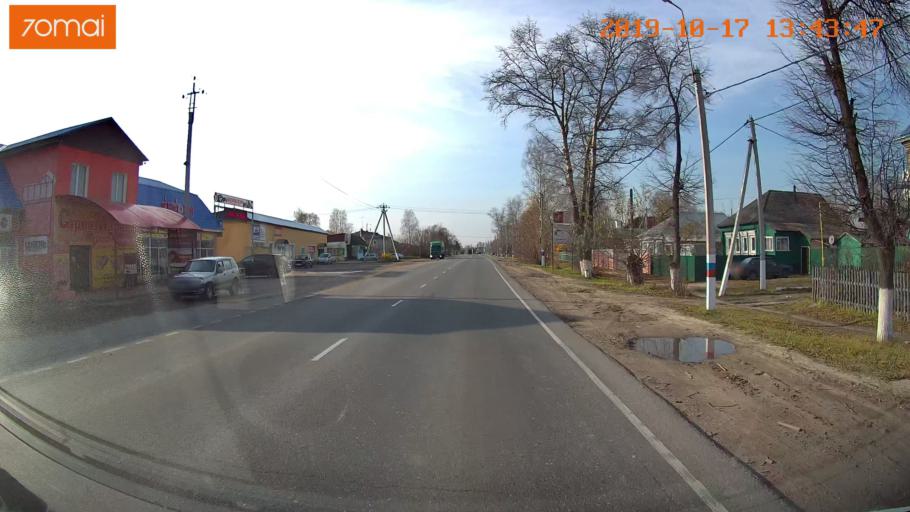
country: RU
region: Rjazan
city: Tuma
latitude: 55.1456
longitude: 40.5381
